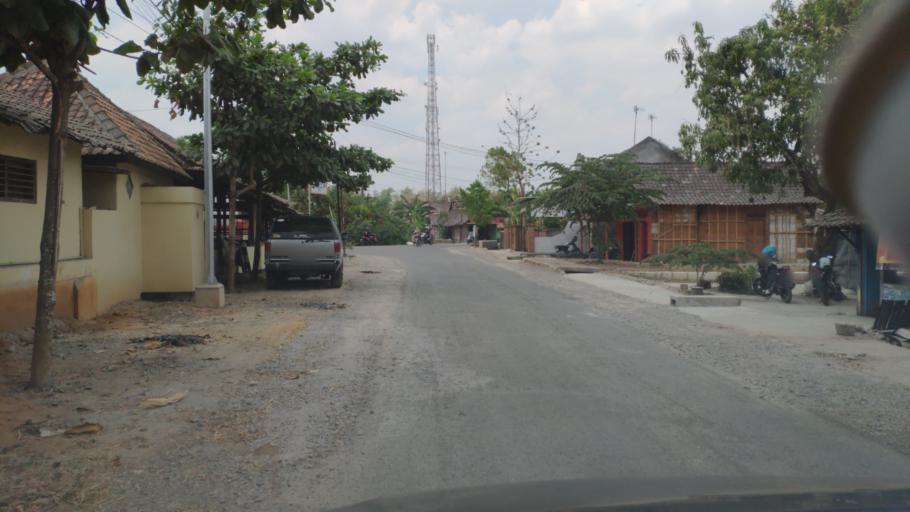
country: ID
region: Central Java
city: Banjarejo
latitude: -7.0323
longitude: 111.3477
